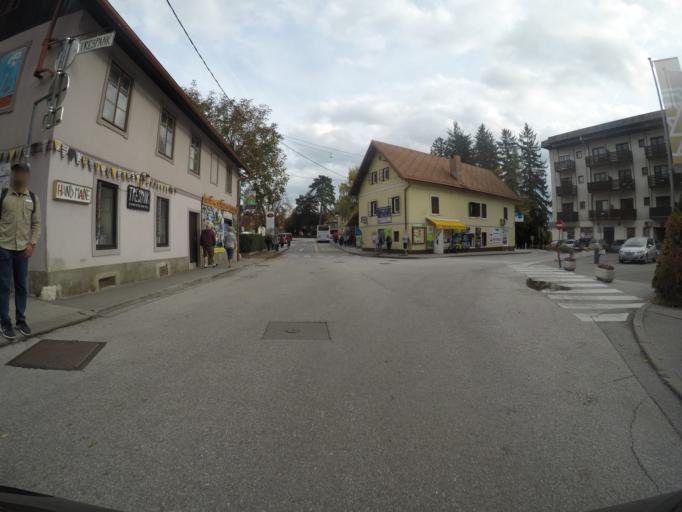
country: SI
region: Bled
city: Bled
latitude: 46.3715
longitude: 14.1063
